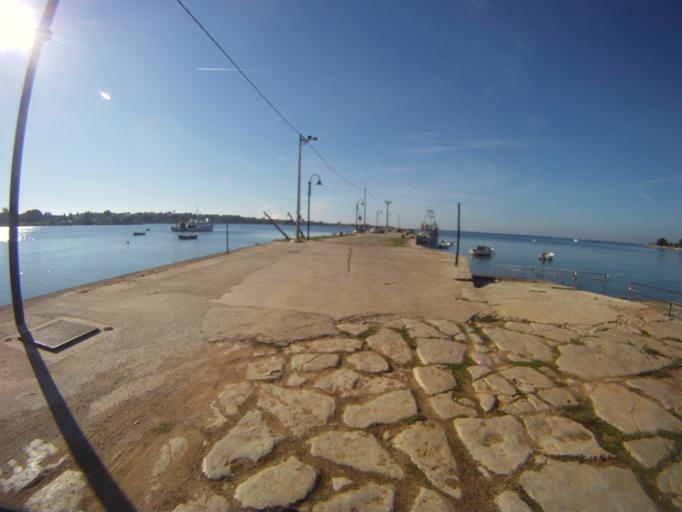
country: HR
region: Istarska
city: Novigrad
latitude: 45.3599
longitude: 13.5527
